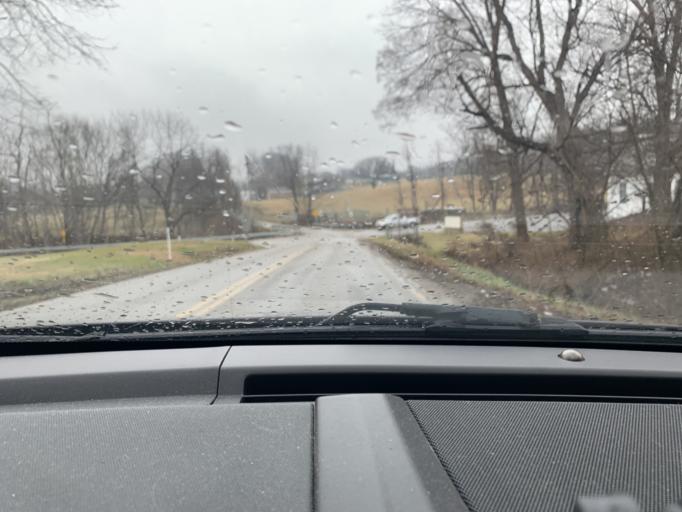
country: US
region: Ohio
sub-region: Ross County
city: Chillicothe
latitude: 39.3813
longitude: -82.9494
